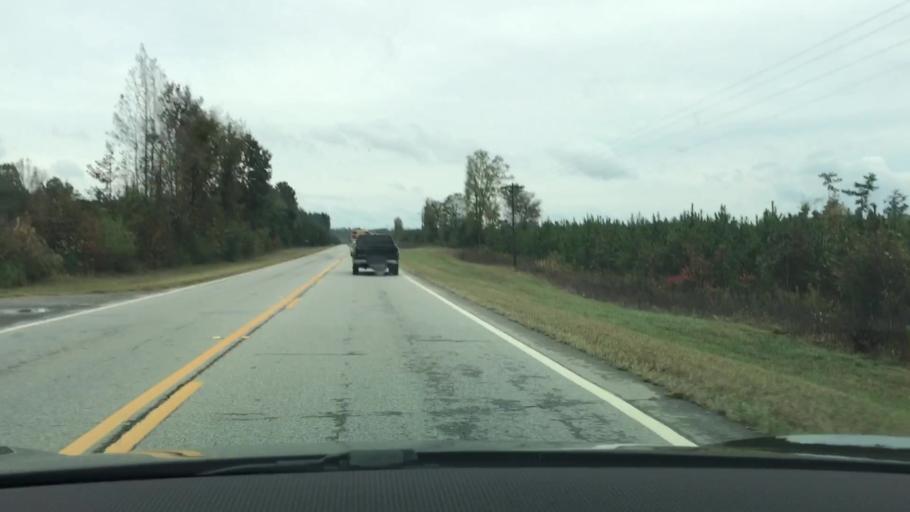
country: US
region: Georgia
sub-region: Greene County
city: Greensboro
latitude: 33.6008
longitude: -83.1973
